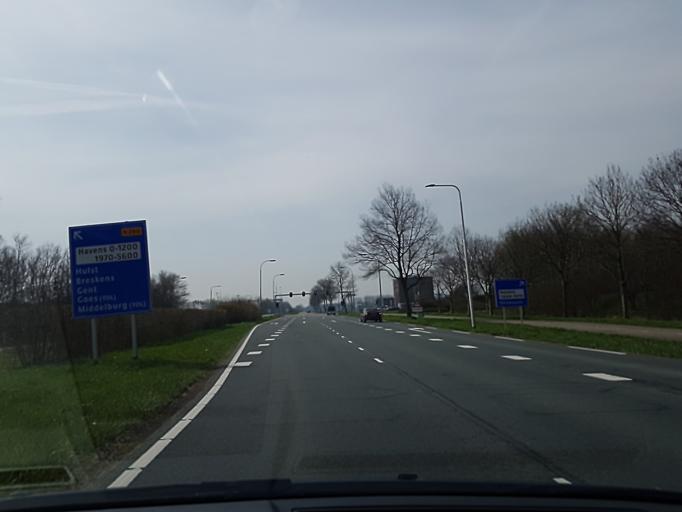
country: NL
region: Zeeland
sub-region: Gemeente Terneuzen
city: Sluiskil
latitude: 51.3052
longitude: 3.8590
